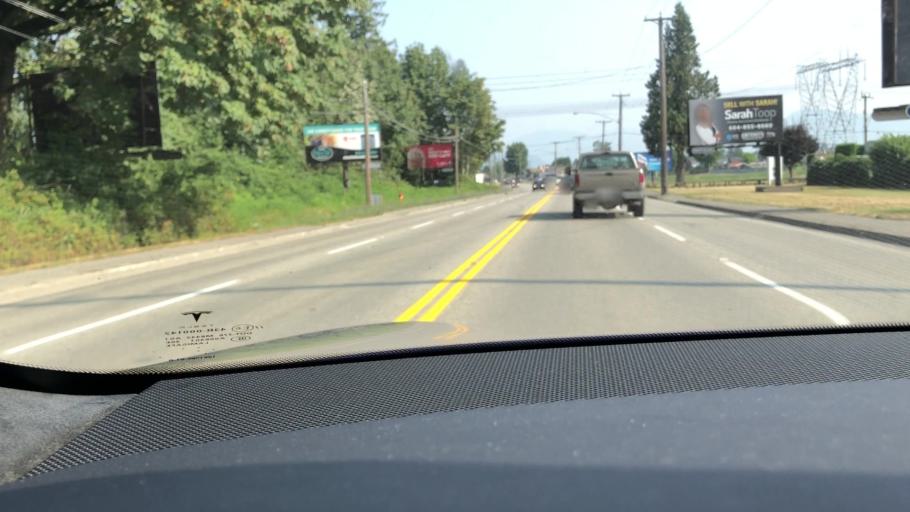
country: CA
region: British Columbia
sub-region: Fraser Valley Regional District
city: Chilliwack
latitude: 49.1134
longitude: -121.9575
